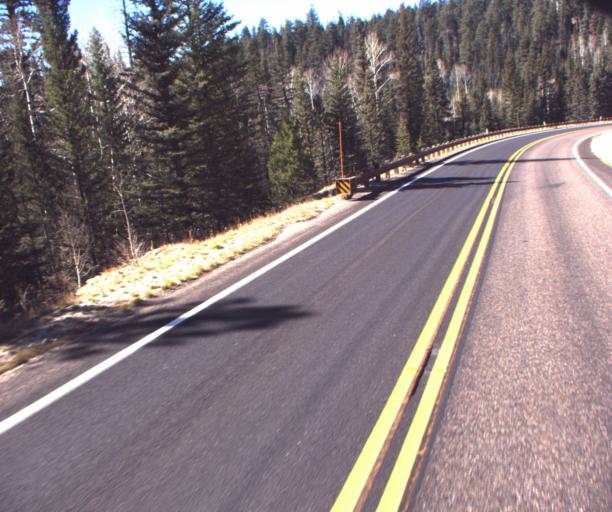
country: US
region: Arizona
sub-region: Coconino County
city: Grand Canyon
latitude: 36.5150
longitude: -112.1398
